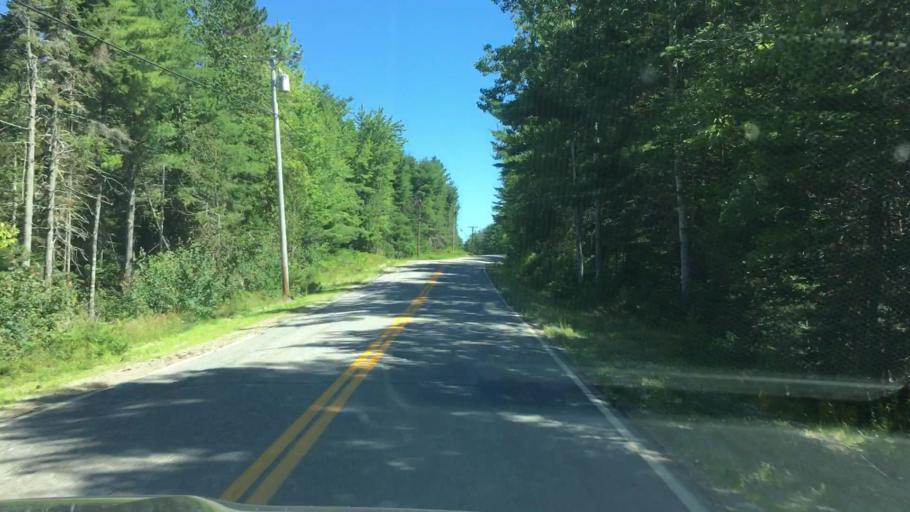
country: US
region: Maine
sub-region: Hancock County
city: Penobscot
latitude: 44.5082
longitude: -68.6756
